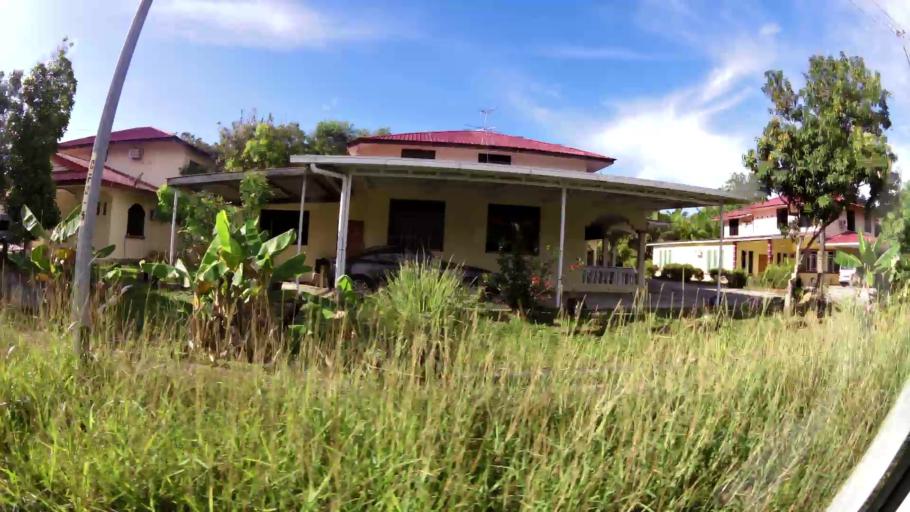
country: BN
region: Brunei and Muara
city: Bandar Seri Begawan
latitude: 4.9703
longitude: 114.9603
